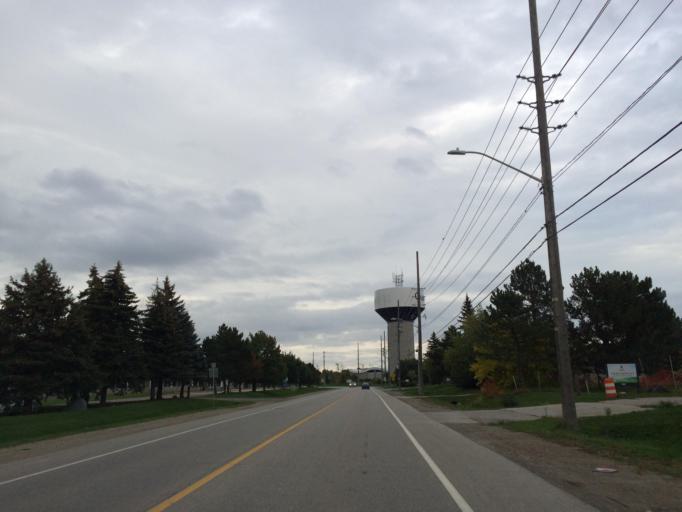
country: CA
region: Ontario
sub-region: Wellington County
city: Guelph
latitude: 43.4935
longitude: -80.2030
